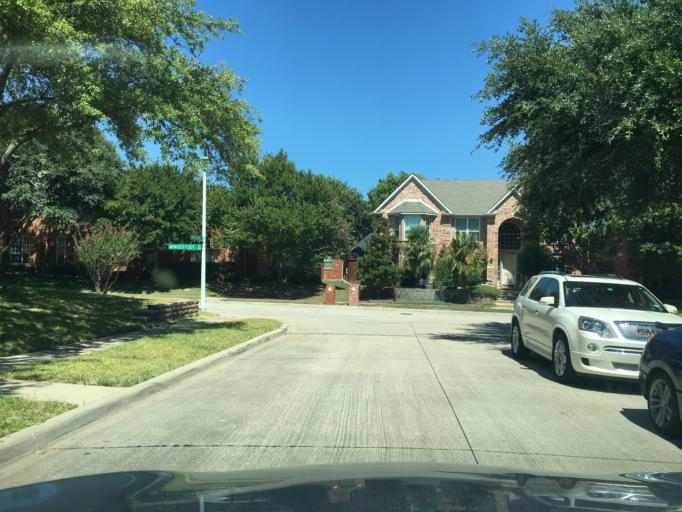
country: US
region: Texas
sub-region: Dallas County
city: Sachse
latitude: 32.9681
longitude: -96.6351
